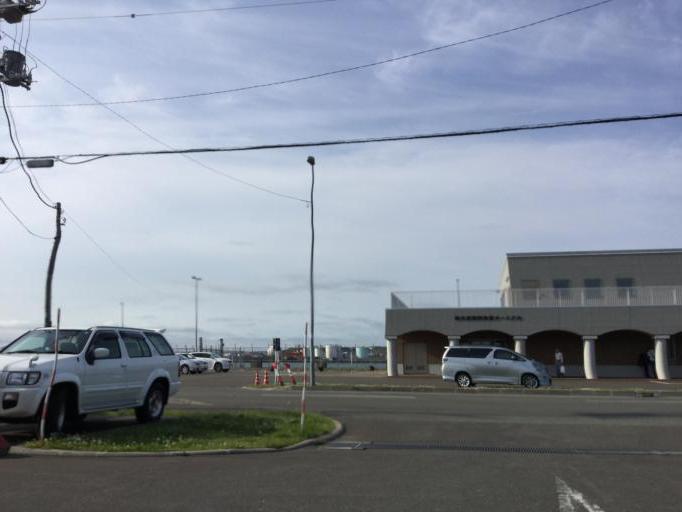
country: JP
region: Hokkaido
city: Wakkanai
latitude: 45.4151
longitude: 141.6833
